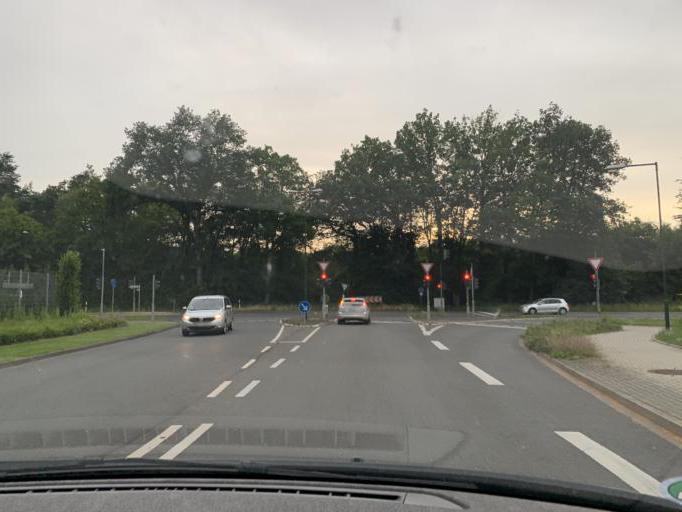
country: DE
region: North Rhine-Westphalia
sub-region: Regierungsbezirk Koln
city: Kerpen
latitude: 50.8825
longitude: 6.6903
